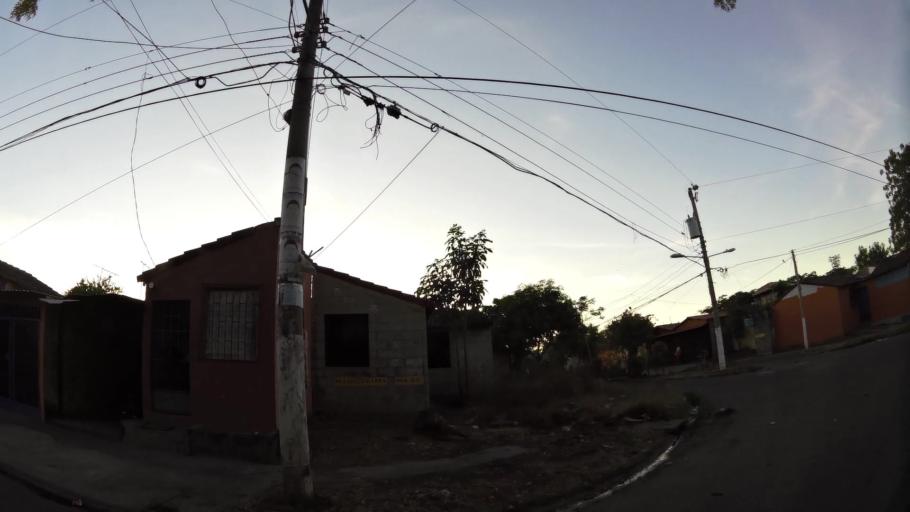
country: SV
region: San Miguel
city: San Miguel
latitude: 13.4798
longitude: -88.1578
